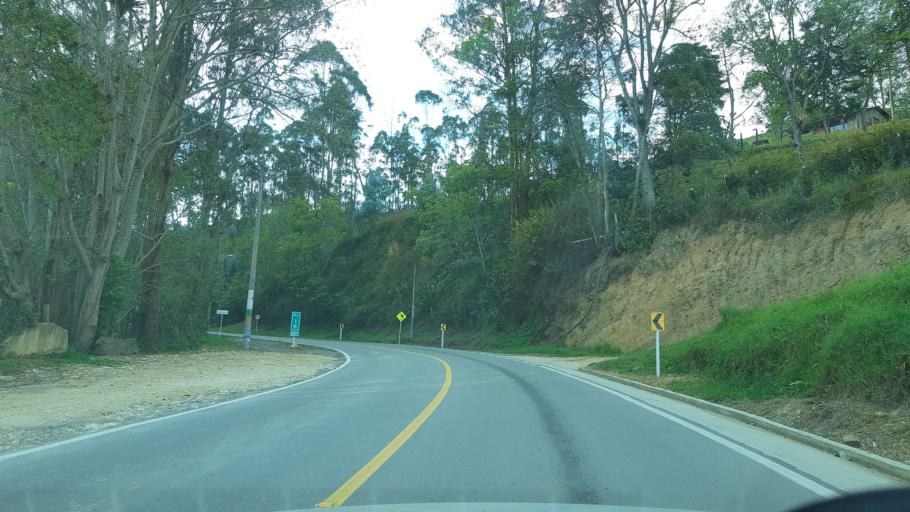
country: CO
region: Cundinamarca
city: Macheta
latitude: 5.0826
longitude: -73.6099
